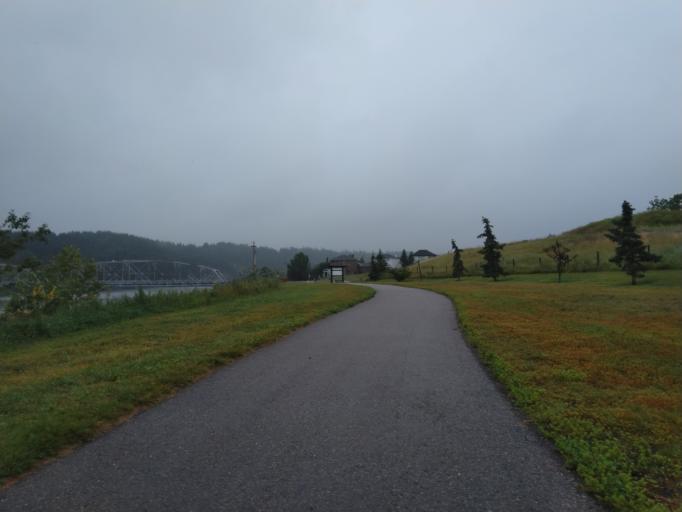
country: CA
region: Alberta
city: Cochrane
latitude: 51.1741
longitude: -114.4641
